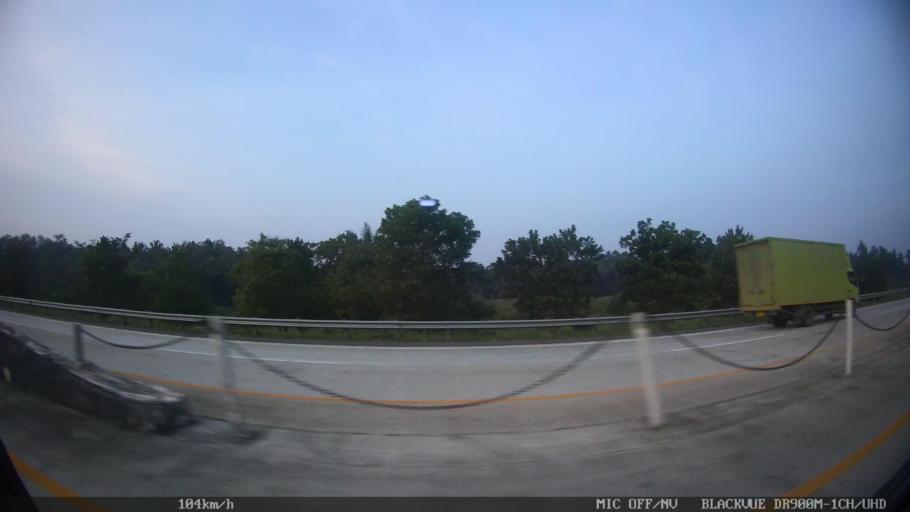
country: ID
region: Lampung
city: Pasuruan
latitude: -5.7061
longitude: 105.6406
